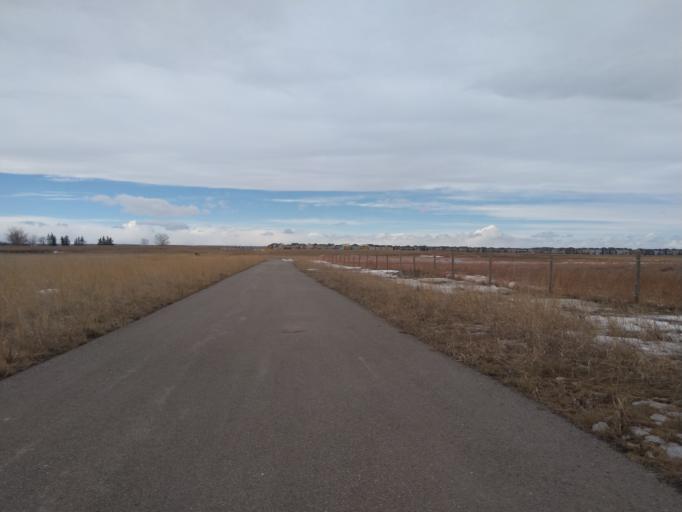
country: CA
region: Alberta
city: Calgary
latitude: 51.1434
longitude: -113.9491
